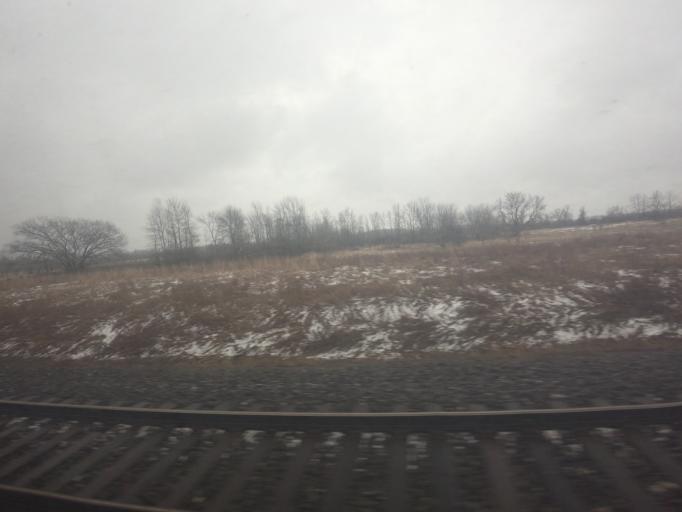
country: CA
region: Ontario
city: Belleville
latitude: 44.2019
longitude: -77.2844
